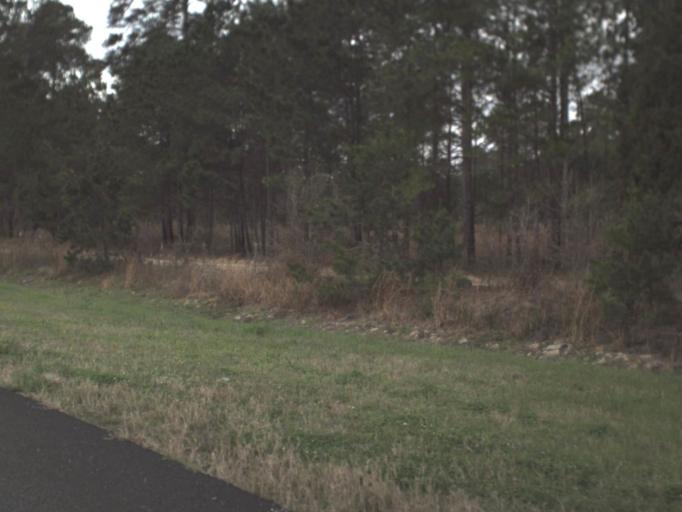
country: US
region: Florida
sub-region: Leon County
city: Tallahassee
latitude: 30.5939
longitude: -84.1896
